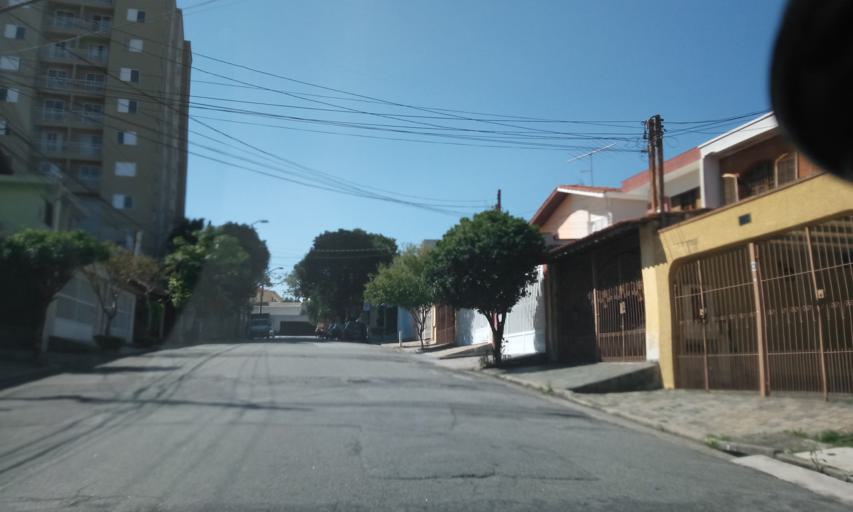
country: BR
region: Sao Paulo
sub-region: Sao Bernardo Do Campo
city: Sao Bernardo do Campo
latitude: -23.7215
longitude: -46.5705
